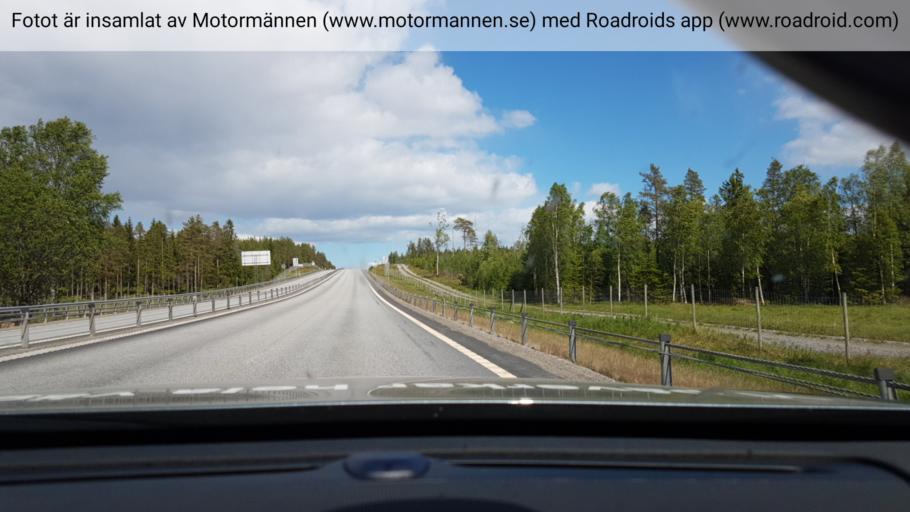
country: SE
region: Vaesterbotten
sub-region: Umea Kommun
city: Hoernefors
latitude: 63.6850
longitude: 20.0071
